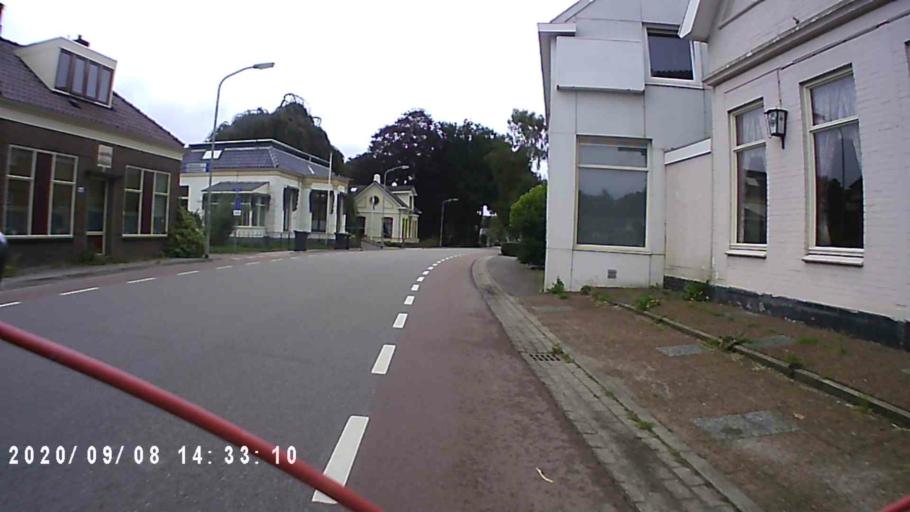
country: NL
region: Groningen
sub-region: Gemeente Slochteren
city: Slochteren
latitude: 53.2341
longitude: 6.8170
